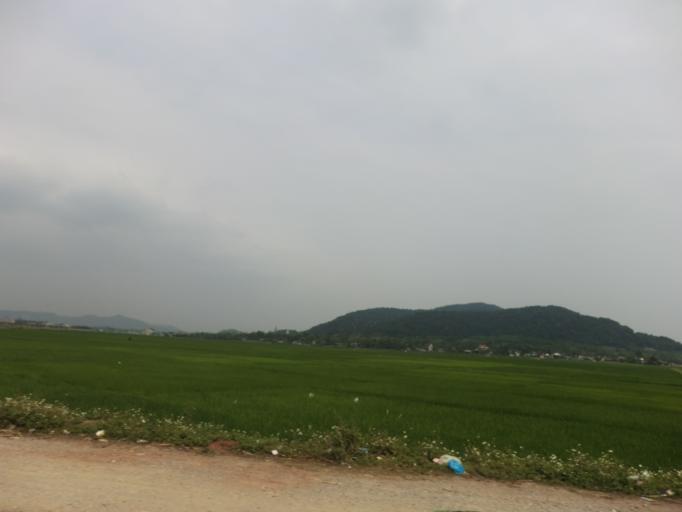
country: VN
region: Nghe An
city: Cau Giat
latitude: 19.3196
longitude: 105.4765
